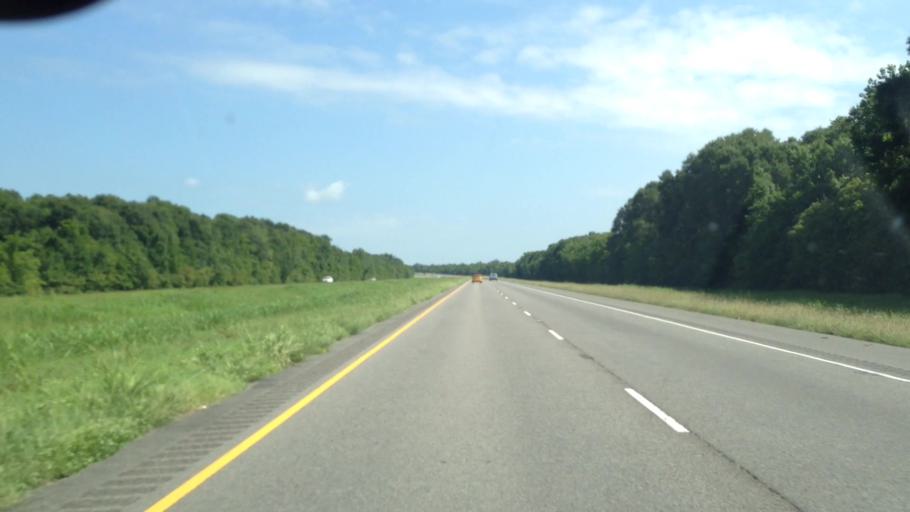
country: US
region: Louisiana
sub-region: Avoyelles Parish
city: Bunkie
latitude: 30.8865
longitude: -92.2270
